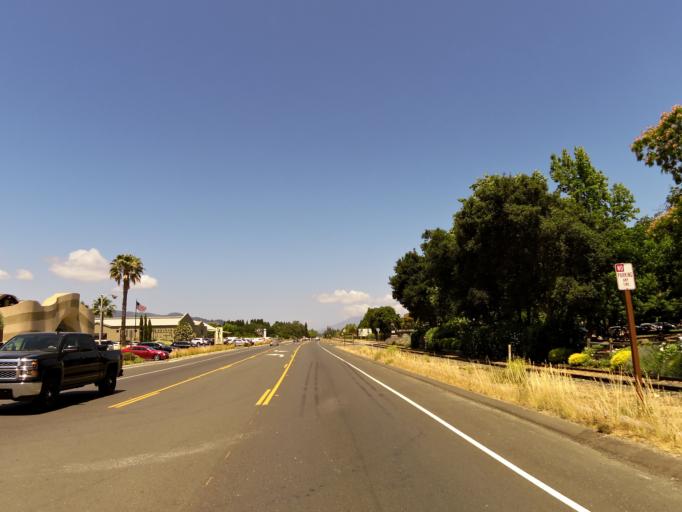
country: US
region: California
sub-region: Napa County
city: Saint Helena
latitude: 38.4880
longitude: -122.4489
